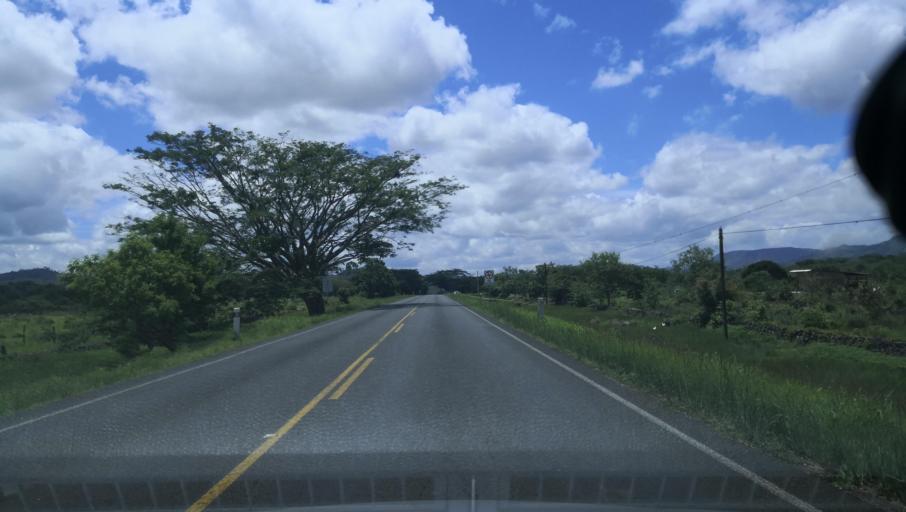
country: NI
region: Esteli
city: Esteli
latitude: 13.2233
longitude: -86.3792
